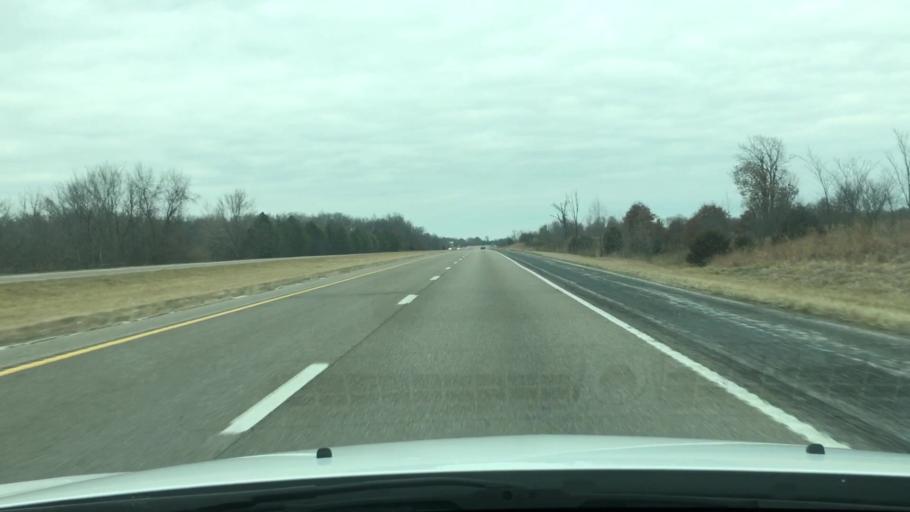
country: US
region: Missouri
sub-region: Callaway County
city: Fulton
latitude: 38.9911
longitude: -91.8936
